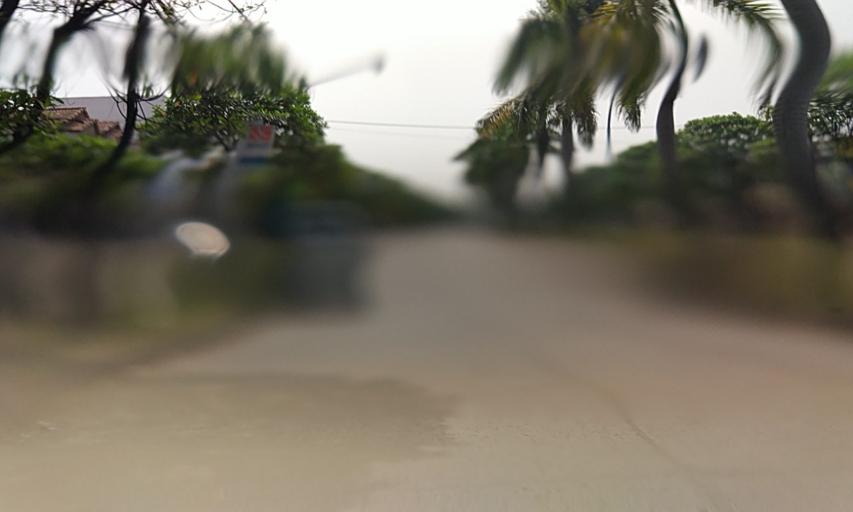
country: ID
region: West Java
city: Margahayukencana
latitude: -6.9561
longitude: 107.5616
